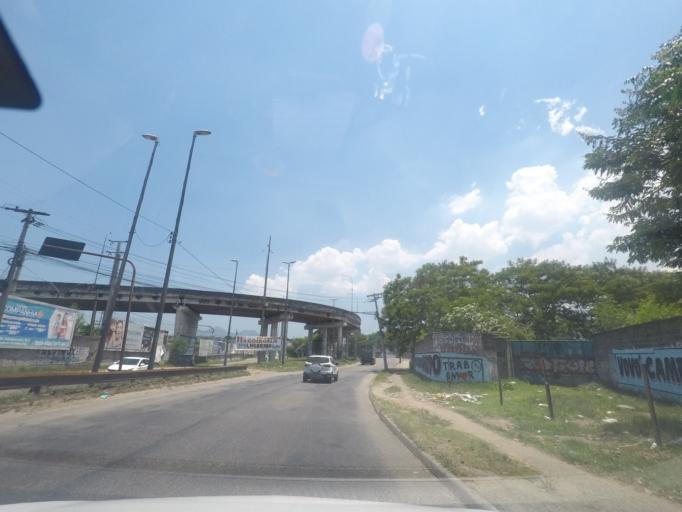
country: BR
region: Rio de Janeiro
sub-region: Duque De Caxias
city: Duque de Caxias
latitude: -22.8011
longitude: -43.3054
